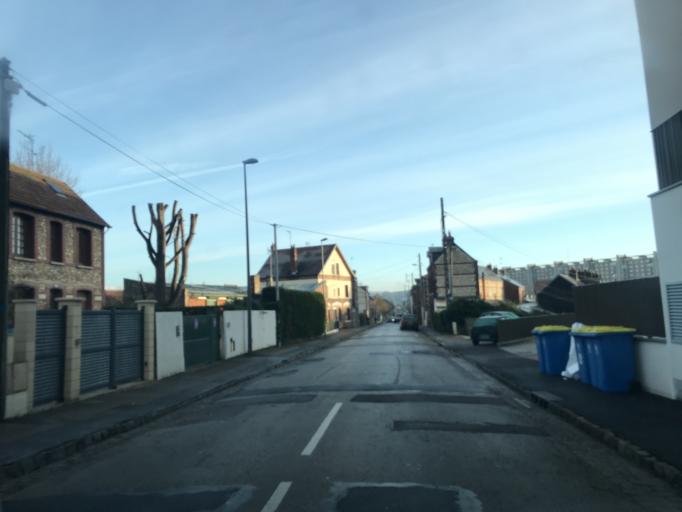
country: FR
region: Haute-Normandie
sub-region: Departement de la Seine-Maritime
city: Sotteville-les-Rouen
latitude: 49.4158
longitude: 1.0864
